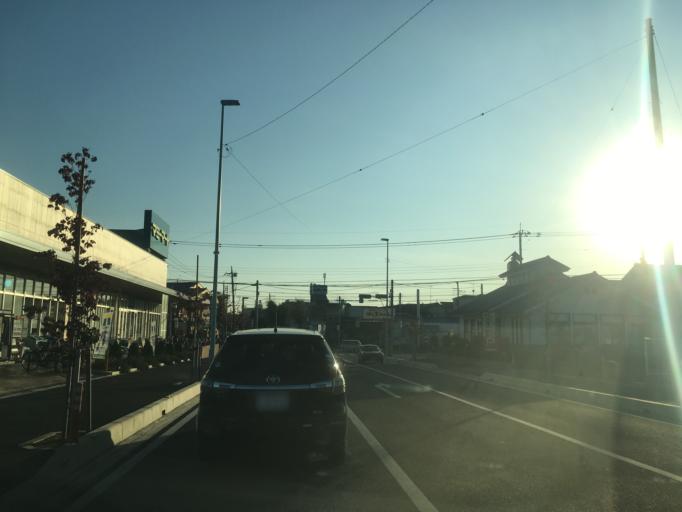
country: JP
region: Saitama
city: Tokorozawa
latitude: 35.8080
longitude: 139.4380
